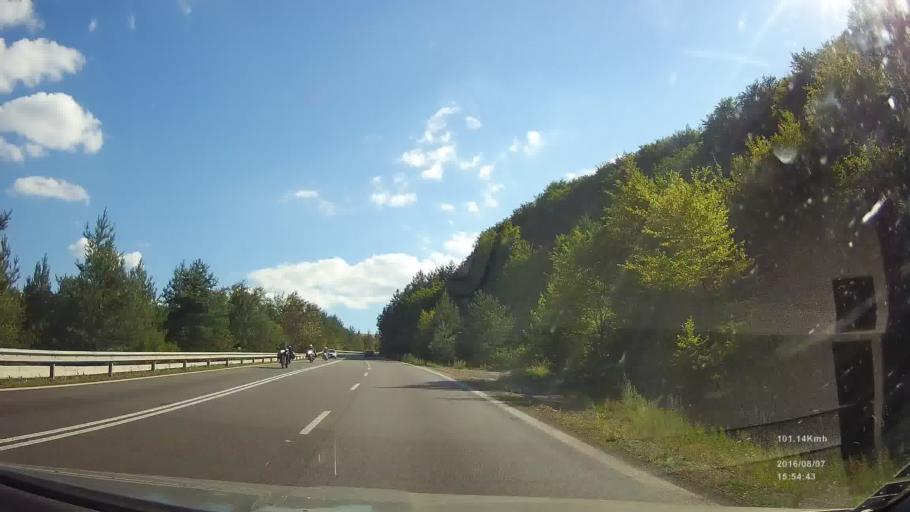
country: SK
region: Presovsky
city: Giraltovce
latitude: 49.0840
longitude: 21.4438
